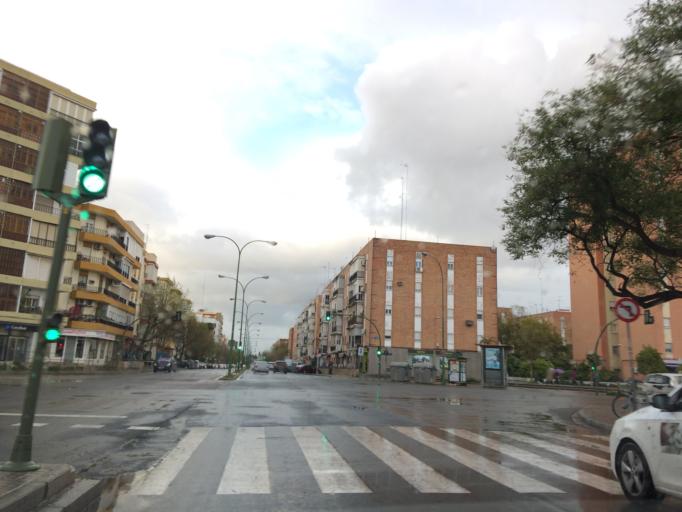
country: ES
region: Andalusia
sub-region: Provincia de Sevilla
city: Sevilla
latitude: 37.4071
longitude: -5.9856
